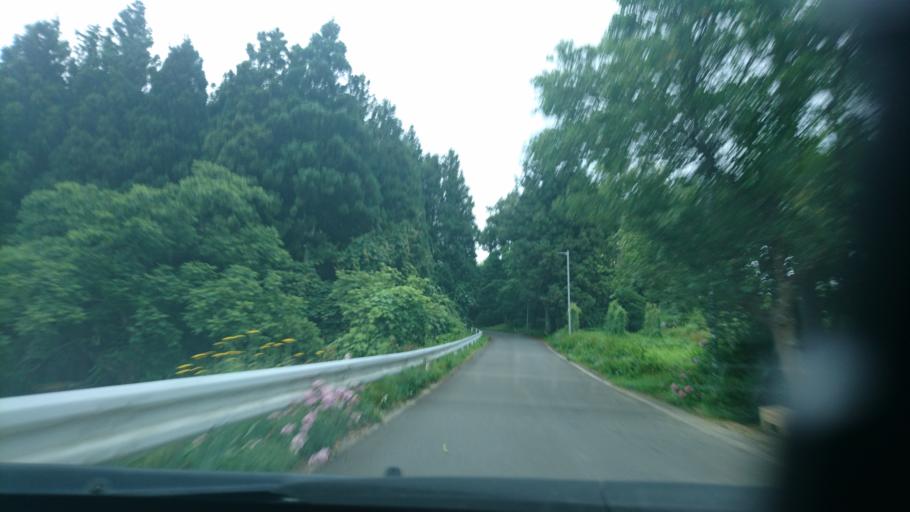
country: JP
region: Iwate
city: Ichinoseki
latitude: 38.8951
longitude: 141.3076
